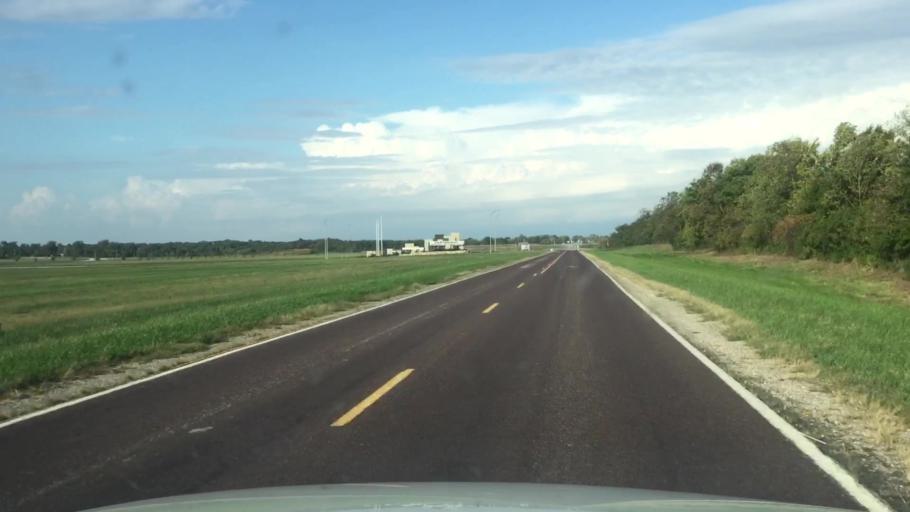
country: US
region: Missouri
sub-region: Boone County
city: Ashland
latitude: 38.8322
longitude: -92.2356
